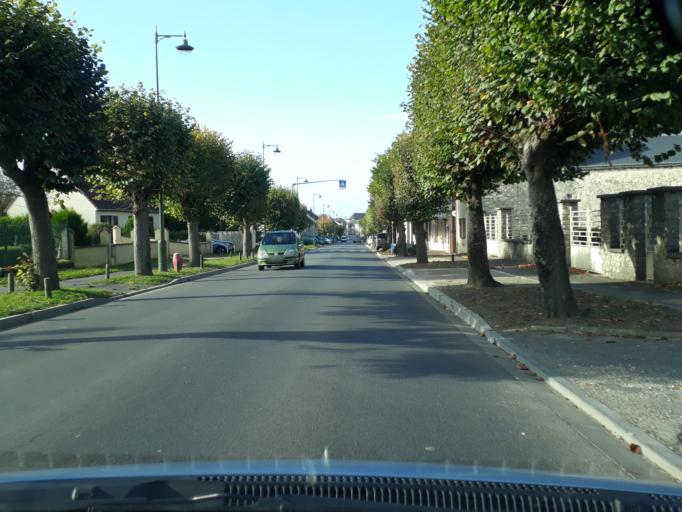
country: FR
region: Ile-de-France
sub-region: Departement de Seine-et-Marne
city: La Chapelle-la-Reine
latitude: 48.3199
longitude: 2.5752
